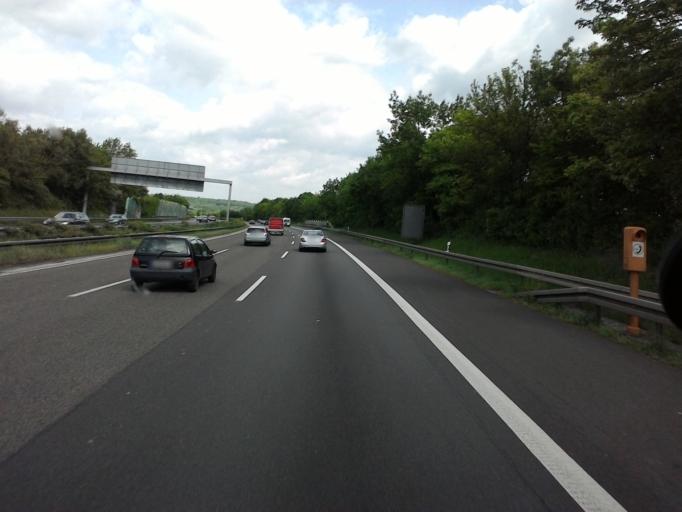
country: DE
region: North Rhine-Westphalia
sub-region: Regierungsbezirk Koln
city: Stossdorf
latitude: 50.7816
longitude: 7.2426
